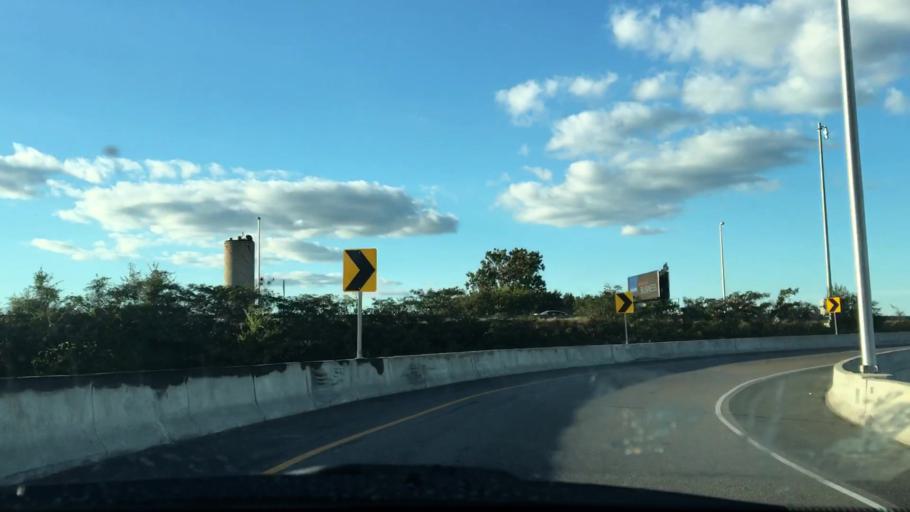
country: US
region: Virginia
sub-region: City of Portsmouth
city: Portsmouth
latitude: 36.8248
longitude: -76.3270
